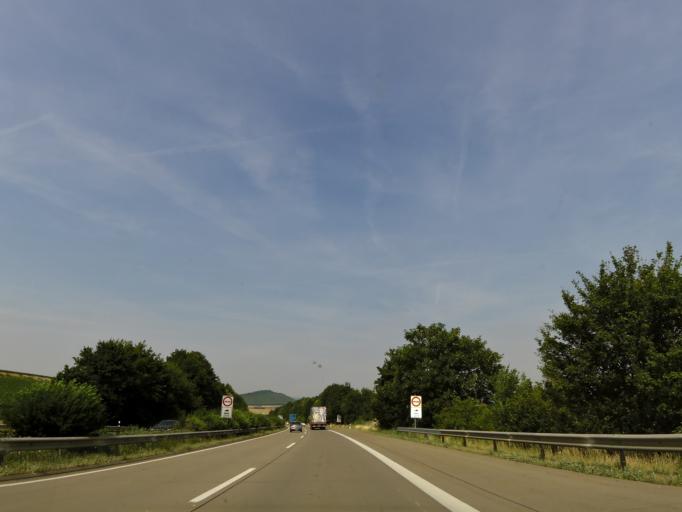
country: DE
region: Rheinland-Pfalz
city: Saffig
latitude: 50.3767
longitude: 7.4052
